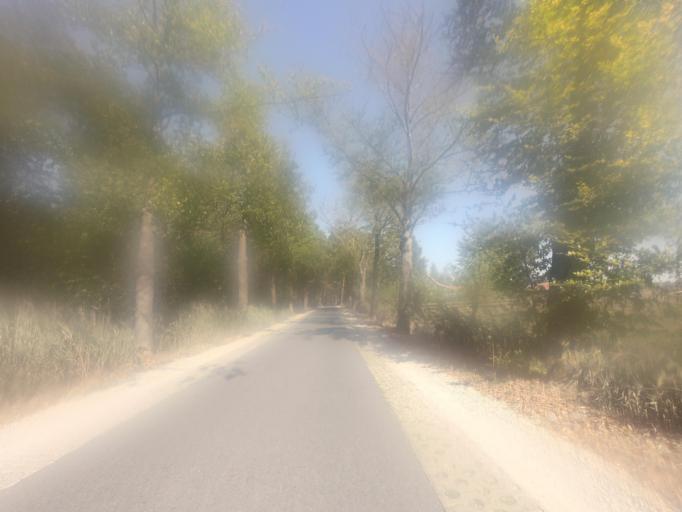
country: NL
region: North Brabant
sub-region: Gemeente Oirschot
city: Oostelbeers
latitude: 51.4942
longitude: 5.2684
